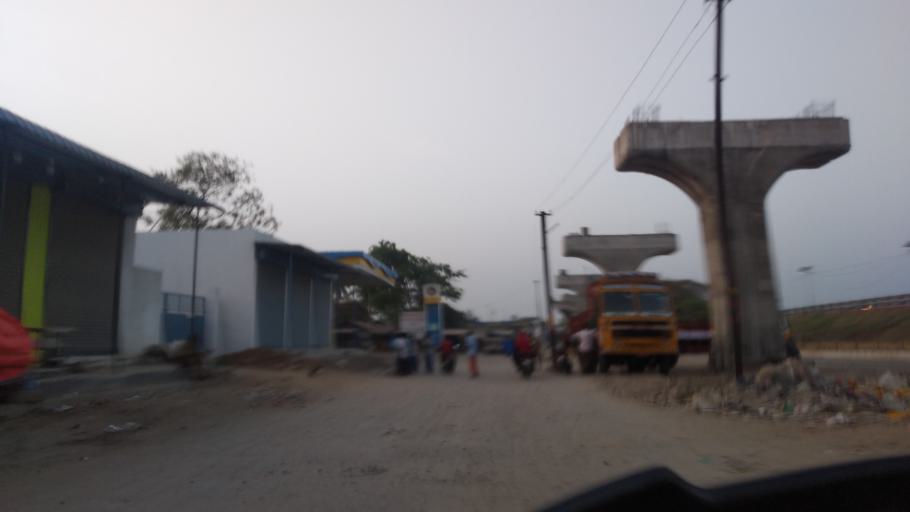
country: IN
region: Tamil Nadu
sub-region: Coimbatore
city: Coimbatore
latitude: 10.9872
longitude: 76.9615
